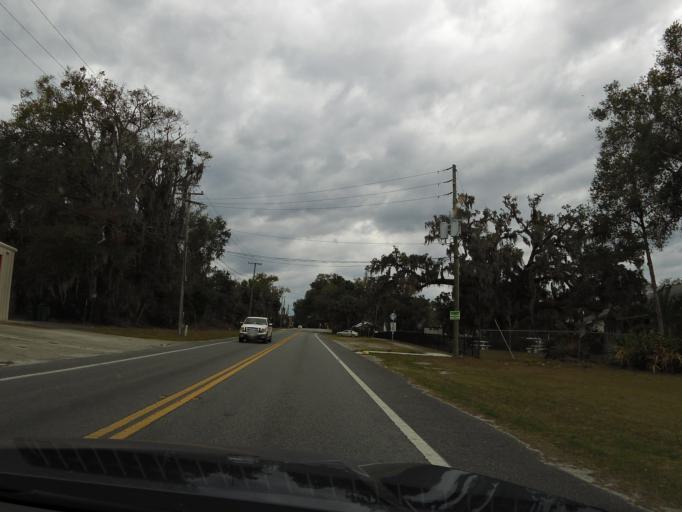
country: US
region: Florida
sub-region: Volusia County
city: Pierson
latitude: 29.3148
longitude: -81.4917
